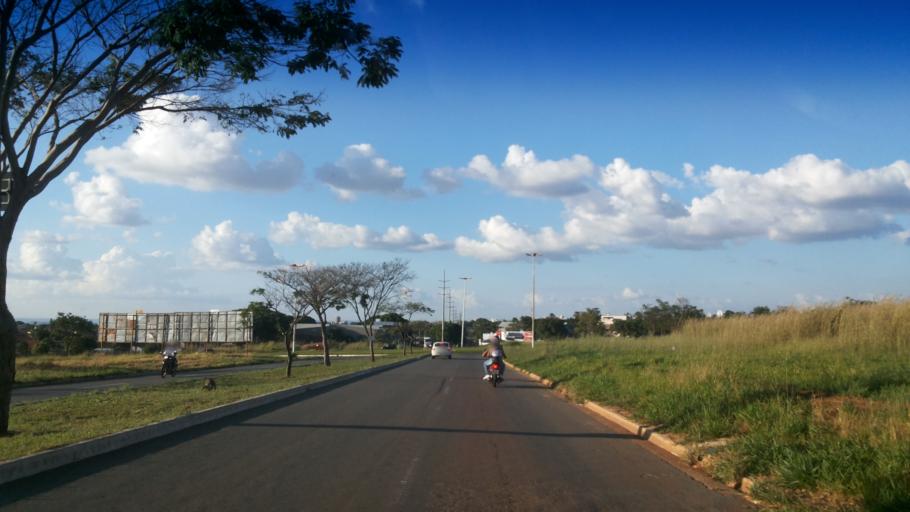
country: BR
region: Goias
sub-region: Goiania
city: Goiania
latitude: -16.7430
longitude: -49.3158
